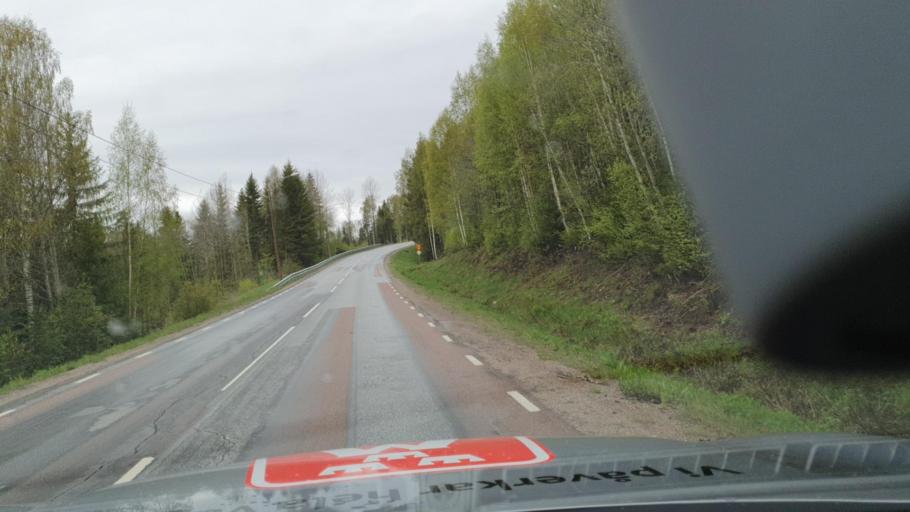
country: SE
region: Vaesternorrland
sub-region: OErnskoeldsviks Kommun
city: Bjasta
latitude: 63.3733
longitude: 18.4817
